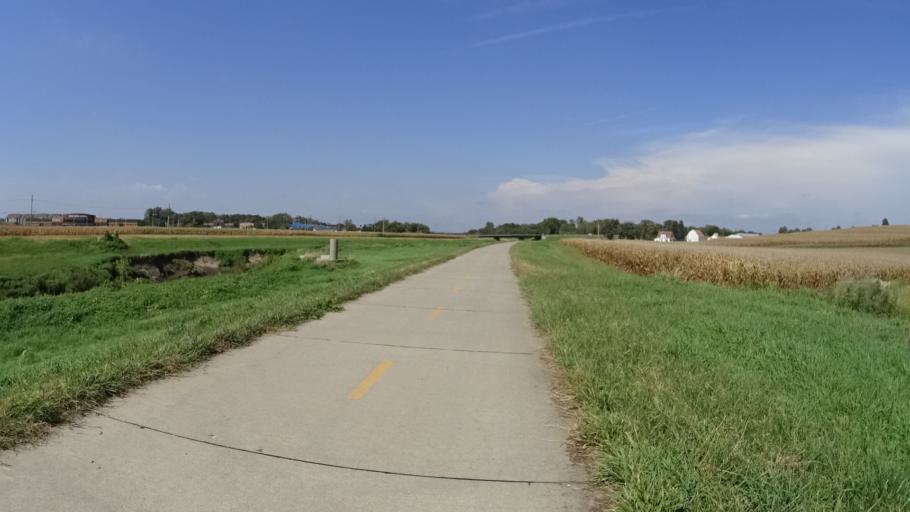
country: US
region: Nebraska
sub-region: Sarpy County
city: Offutt Air Force Base
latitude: 41.1456
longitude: -95.9640
